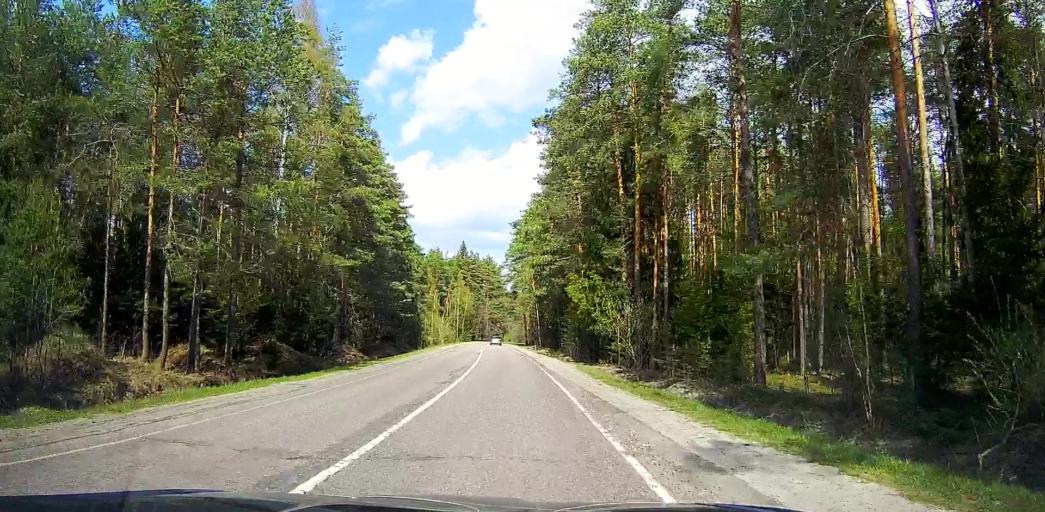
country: RU
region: Moskovskaya
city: Davydovo
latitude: 55.5676
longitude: 38.8218
